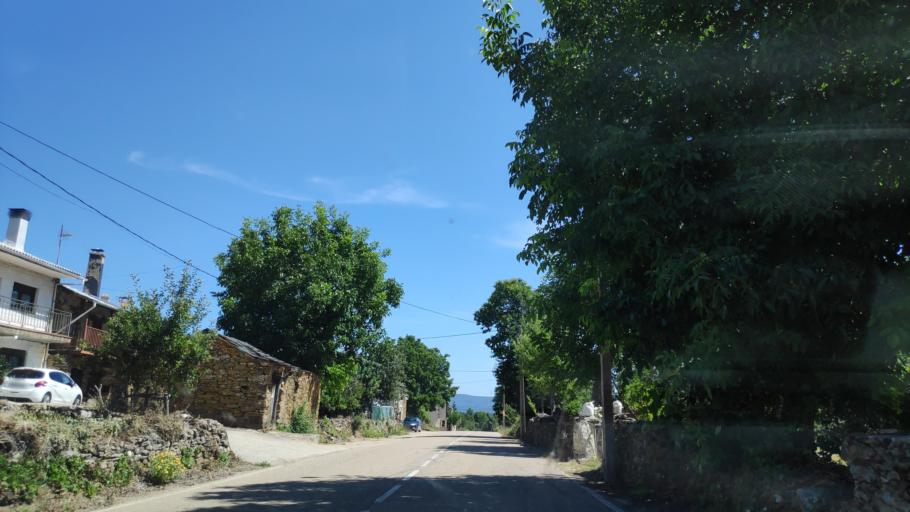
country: ES
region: Castille and Leon
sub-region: Provincia de Zamora
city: Puebla de Sanabria
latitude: 42.0355
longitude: -6.6724
